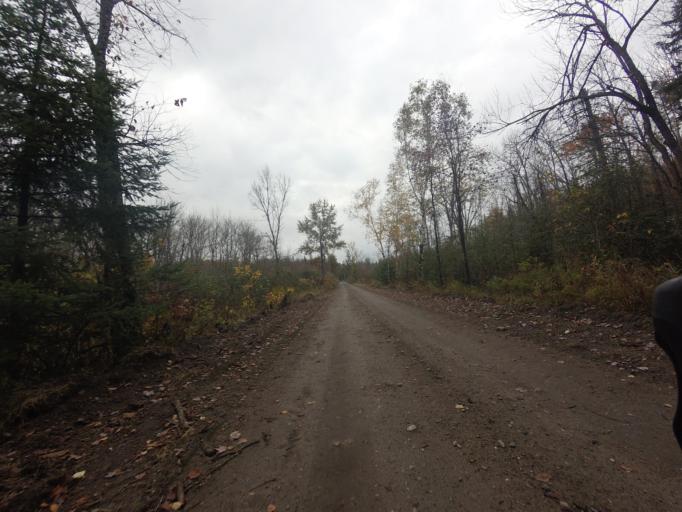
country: CA
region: Ontario
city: Renfrew
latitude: 45.1741
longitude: -76.6816
